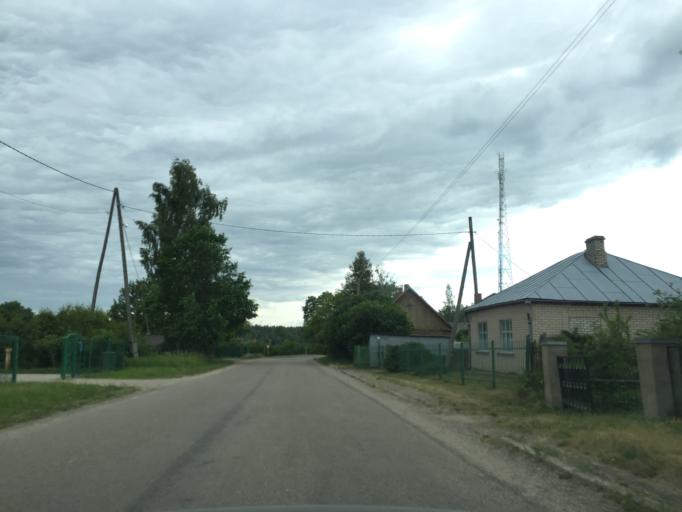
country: LV
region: Vilanu
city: Vilani
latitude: 56.5415
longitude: 26.9291
